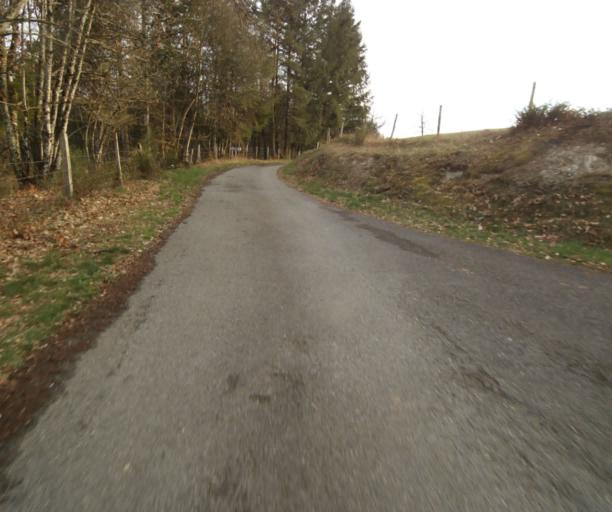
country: FR
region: Limousin
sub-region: Departement de la Correze
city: Argentat
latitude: 45.2247
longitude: 1.9458
